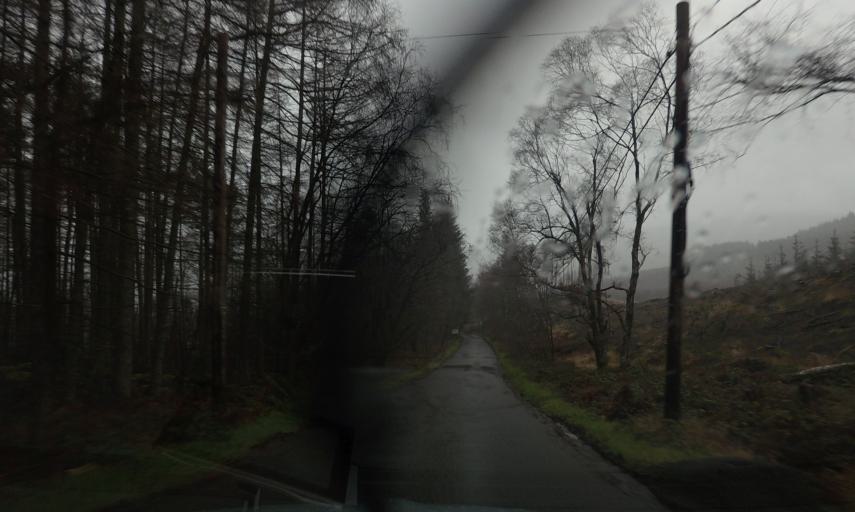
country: GB
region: Scotland
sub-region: West Dunbartonshire
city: Balloch
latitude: 56.1467
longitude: -4.6390
